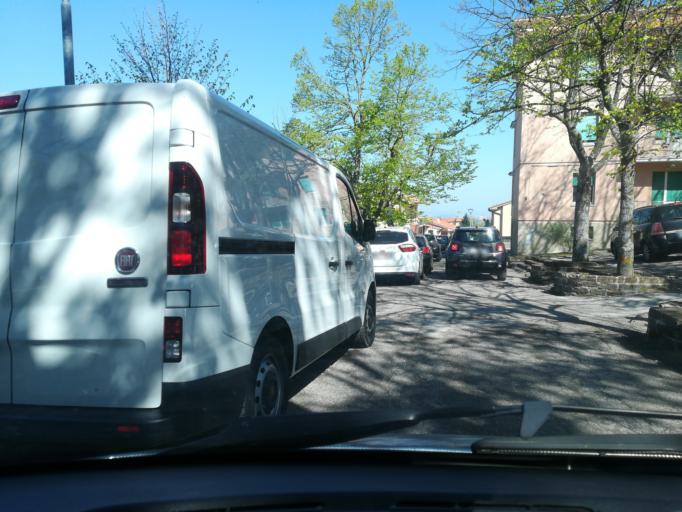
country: IT
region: The Marches
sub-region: Provincia di Macerata
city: Cingoli
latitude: 43.3761
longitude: 13.2099
